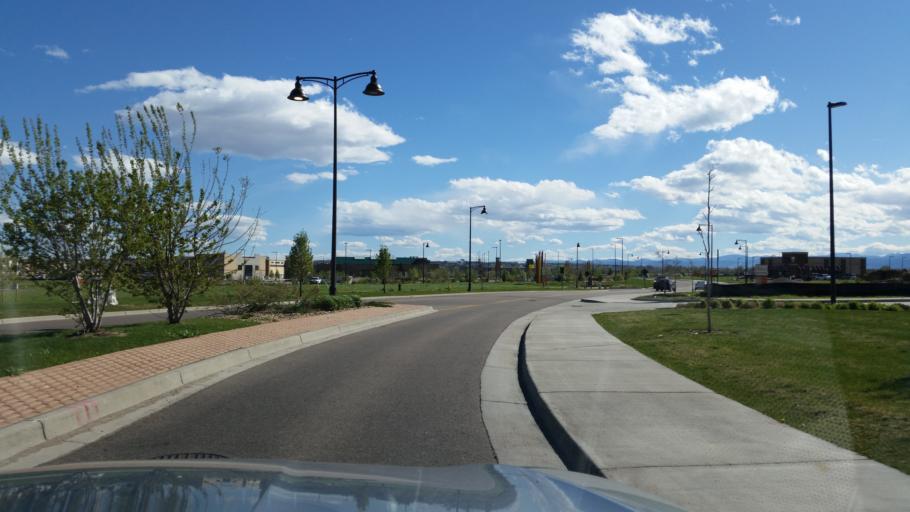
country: US
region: Colorado
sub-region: Adams County
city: Northglenn
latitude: 39.9566
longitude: -104.9846
